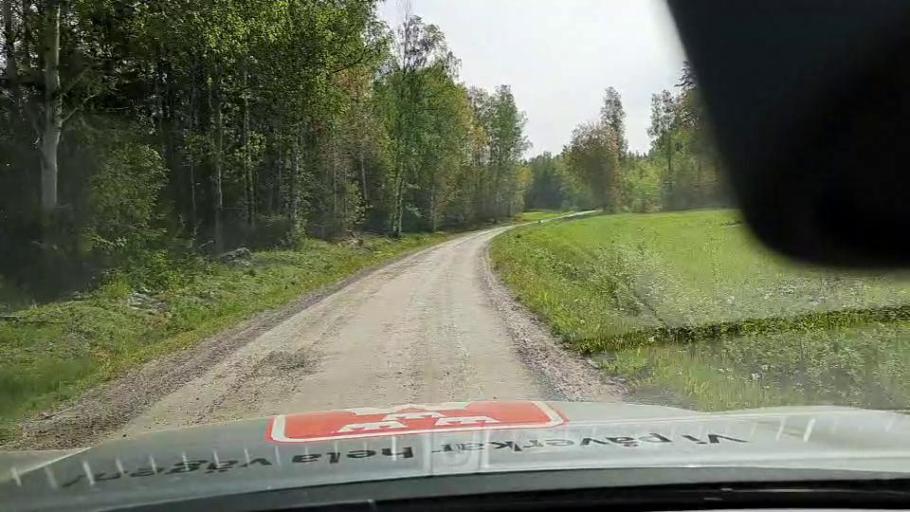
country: SE
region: Soedermanland
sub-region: Eskilstuna Kommun
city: Arla
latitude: 59.2614
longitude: 16.8035
